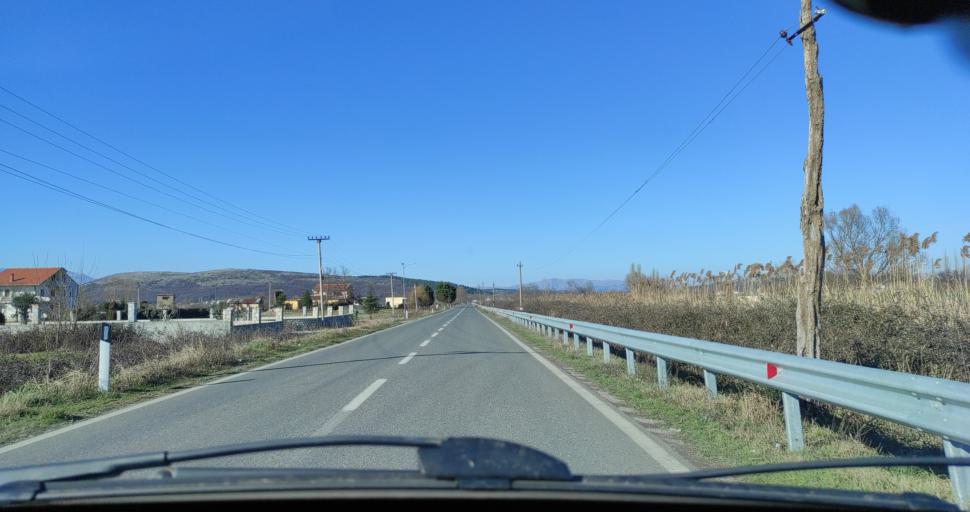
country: AL
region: Shkoder
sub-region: Rrethi i Shkodres
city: Velipoje
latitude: 41.8886
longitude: 19.4034
